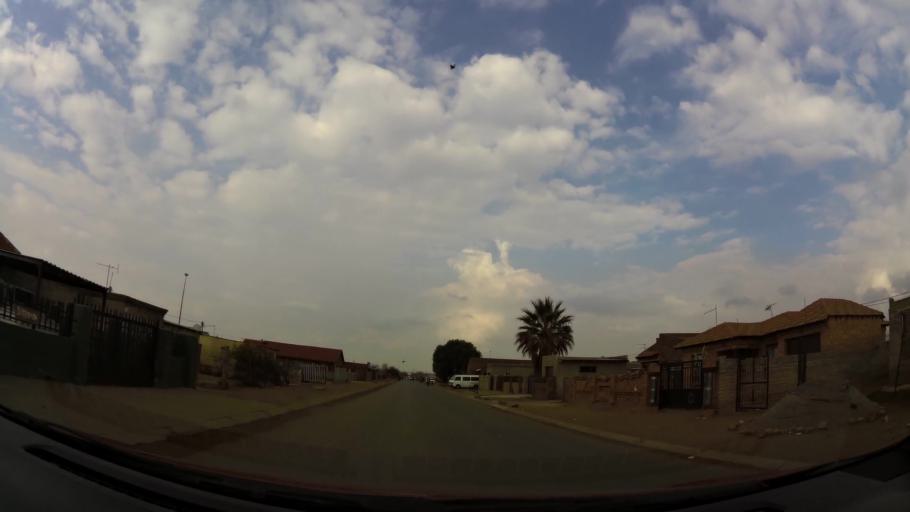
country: ZA
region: Gauteng
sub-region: Sedibeng District Municipality
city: Vanderbijlpark
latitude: -26.6742
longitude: 27.8572
